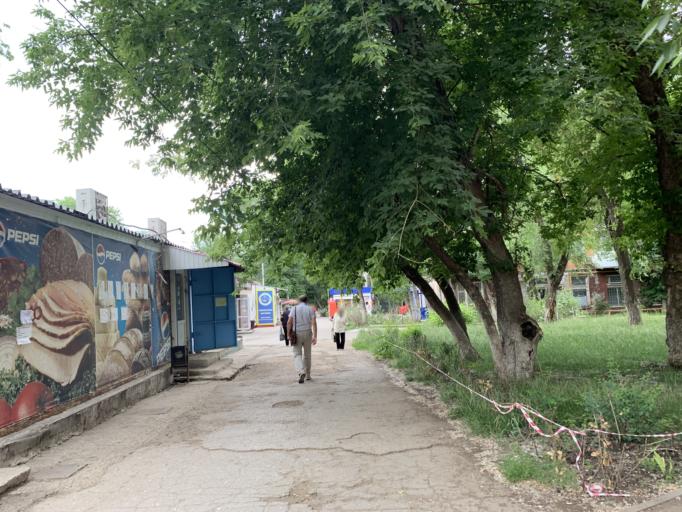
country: RU
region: Samara
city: Samara
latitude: 53.2111
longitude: 50.1716
